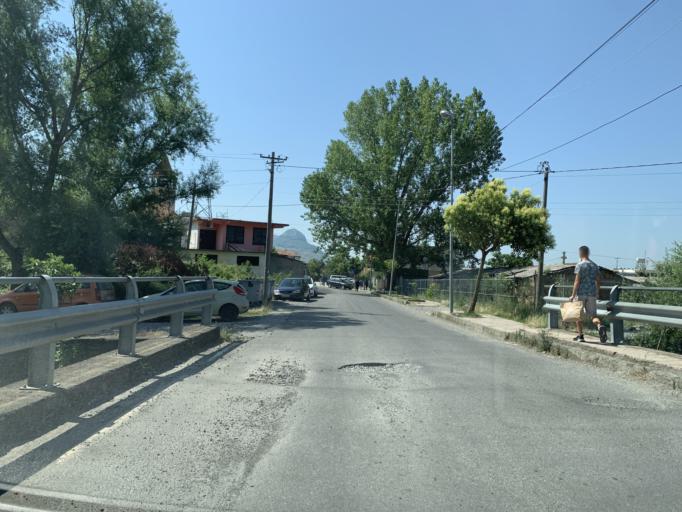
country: AL
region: Shkoder
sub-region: Rrethi i Shkodres
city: Vau i Dejes
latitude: 42.0085
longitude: 19.6399
